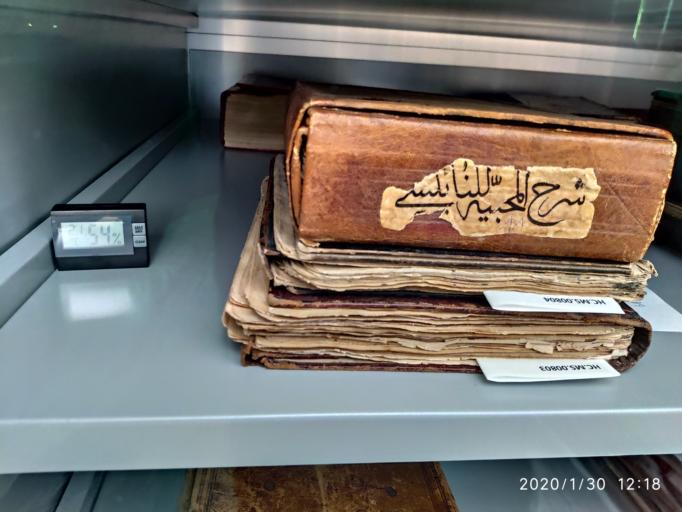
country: QA
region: Baladiyat ar Rayyan
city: Ar Rayyan
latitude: 25.3179
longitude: 51.4414
